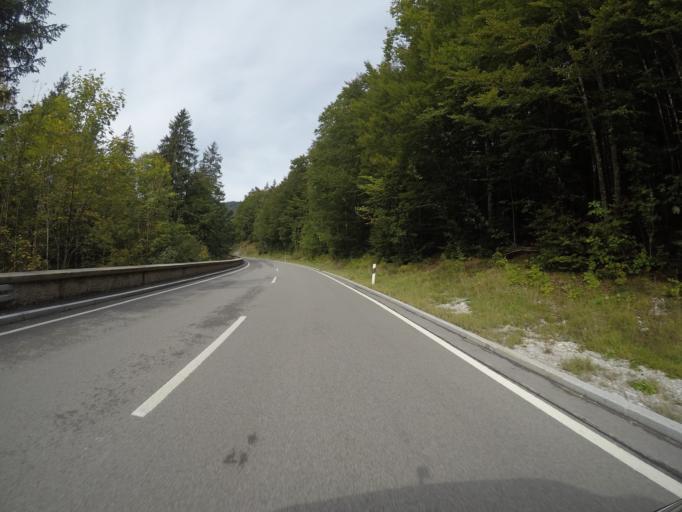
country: DE
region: Bavaria
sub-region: Upper Bavaria
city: Lenggries
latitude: 47.5832
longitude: 11.6076
